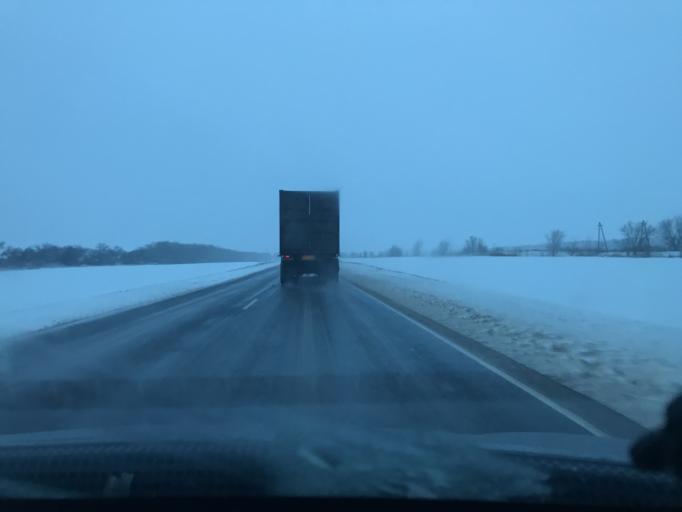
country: RU
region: Rostov
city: Letnik
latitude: 46.0450
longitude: 41.2110
